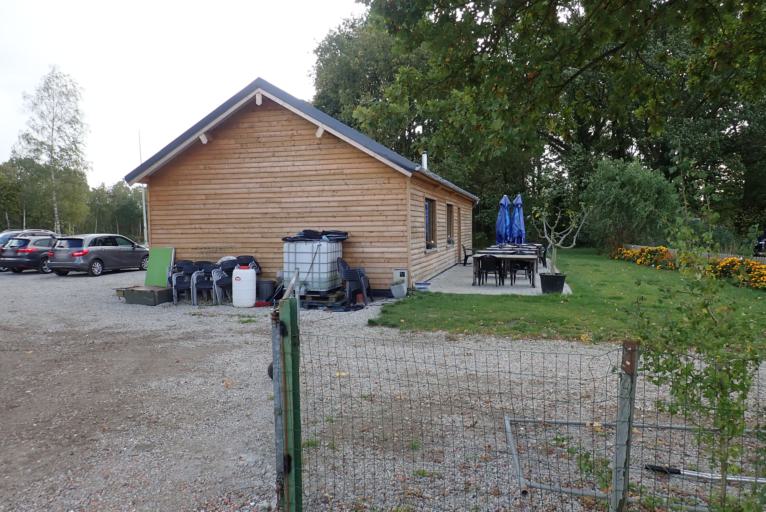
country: BE
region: Flanders
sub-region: Provincie Antwerpen
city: Duffel
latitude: 51.0648
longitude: 4.5019
